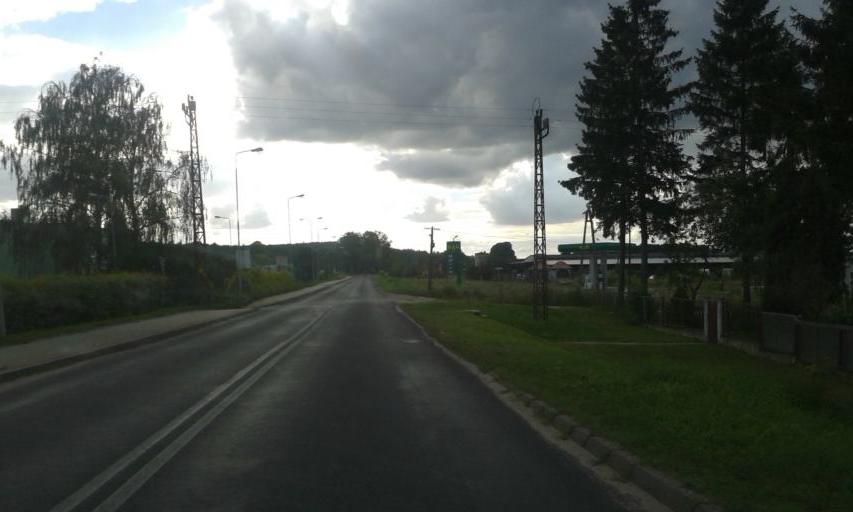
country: PL
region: West Pomeranian Voivodeship
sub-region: Powiat szczecinecki
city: Barwice
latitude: 53.7450
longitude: 16.3482
